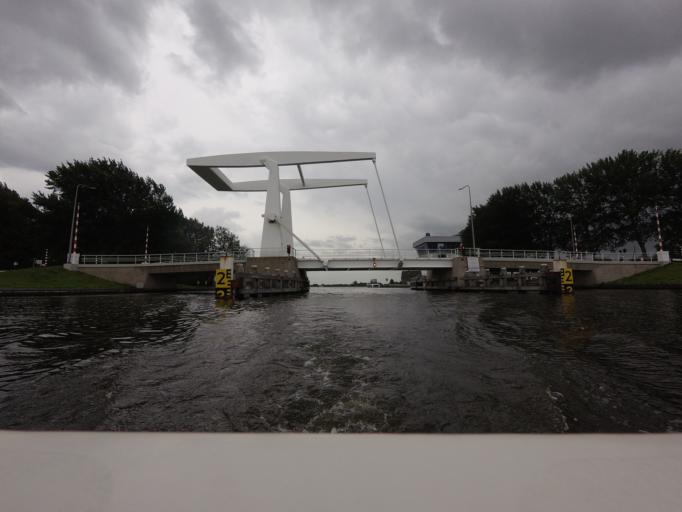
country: NL
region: Friesland
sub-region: Gemeente Smallingerland
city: Oudega
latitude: 53.1051
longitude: 5.9495
